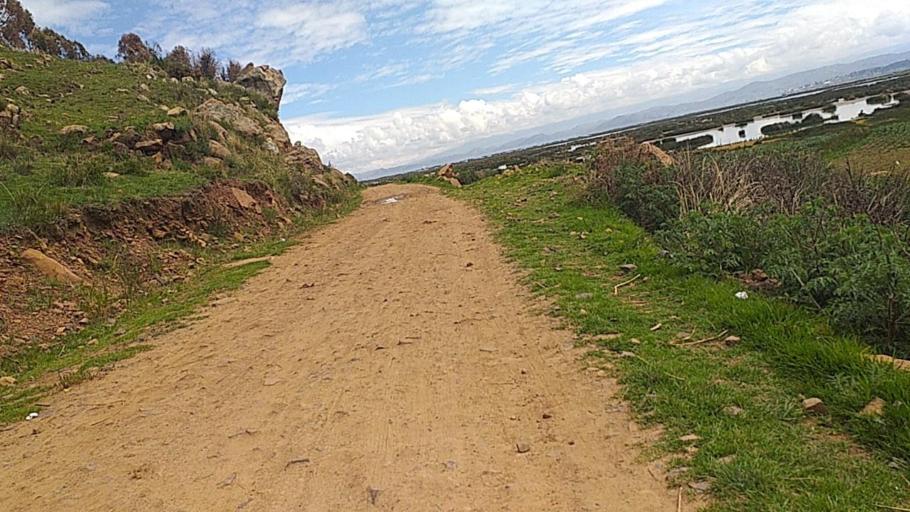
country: BO
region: La Paz
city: Batallas
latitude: -16.3349
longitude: -68.6380
